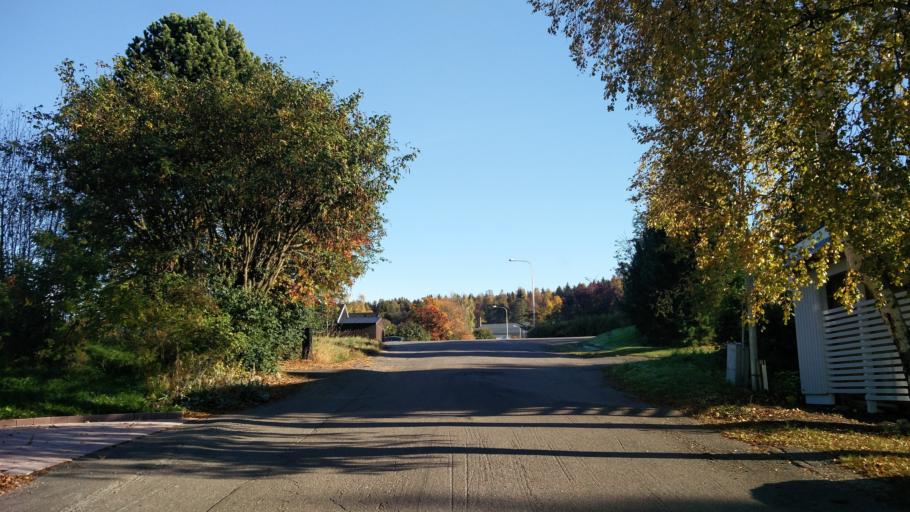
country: SE
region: Vaesternorrland
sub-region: Sundsvalls Kommun
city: Sundsvall
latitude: 62.4006
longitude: 17.2628
